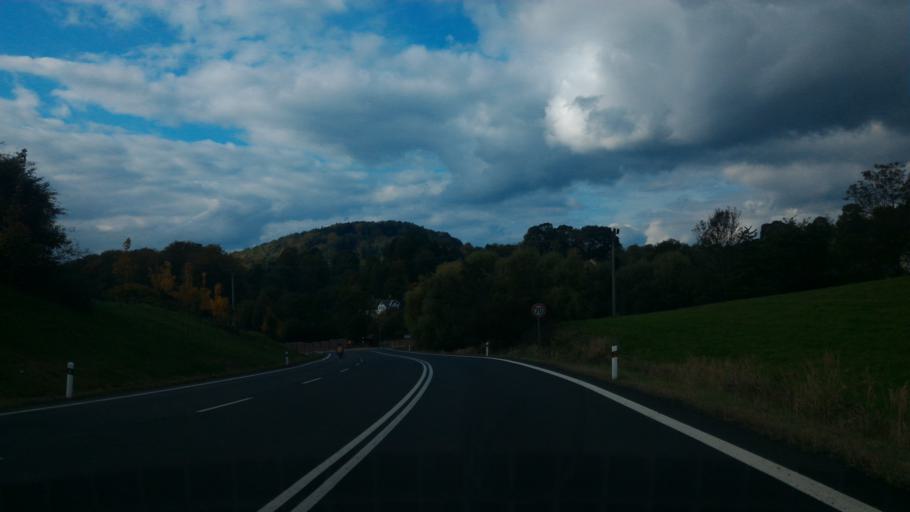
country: CZ
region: Ustecky
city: Ceska Kamenice
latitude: 50.8169
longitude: 14.4534
